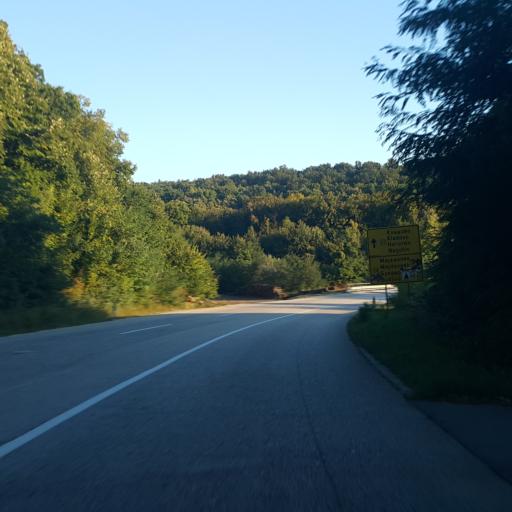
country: RS
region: Central Serbia
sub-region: Borski Okrug
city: Negotin
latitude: 44.2180
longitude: 22.4884
